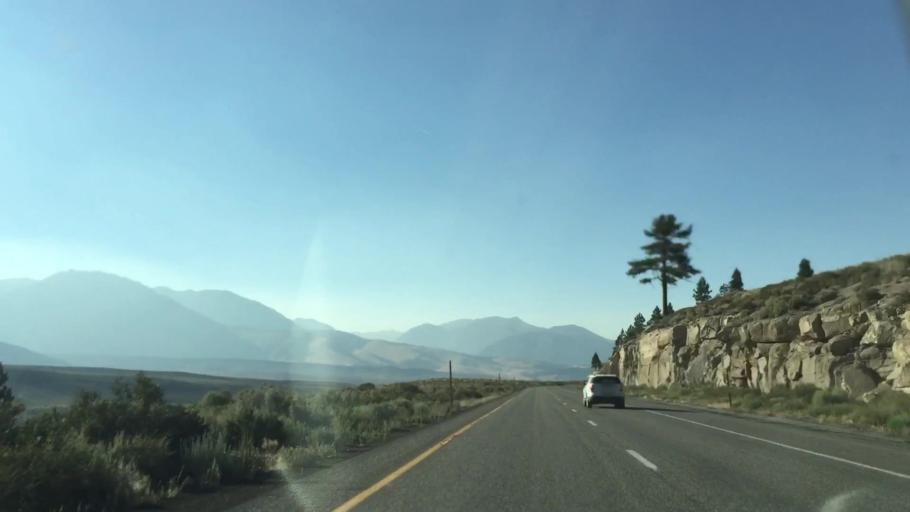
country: US
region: California
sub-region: Mono County
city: Mammoth Lakes
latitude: 37.8279
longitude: -119.0656
